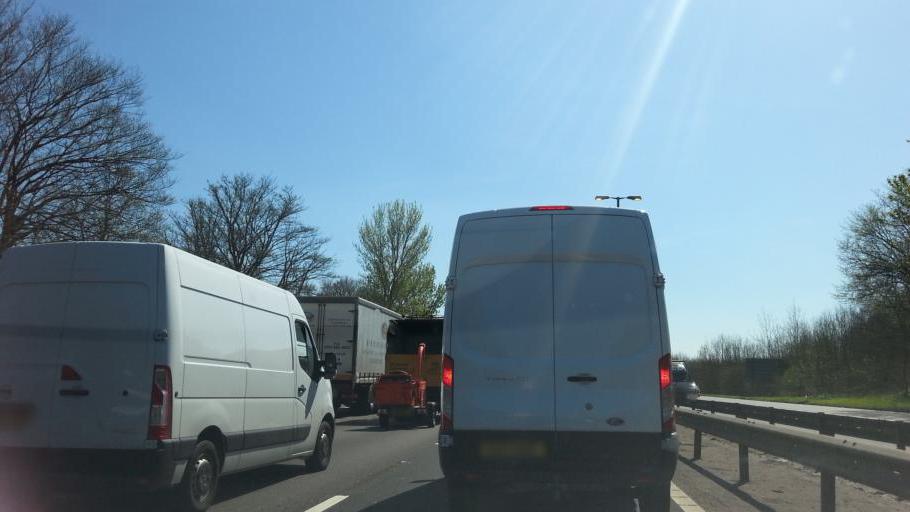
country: GB
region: England
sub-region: Sandwell
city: West Bromwich
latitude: 52.5329
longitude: -1.9710
